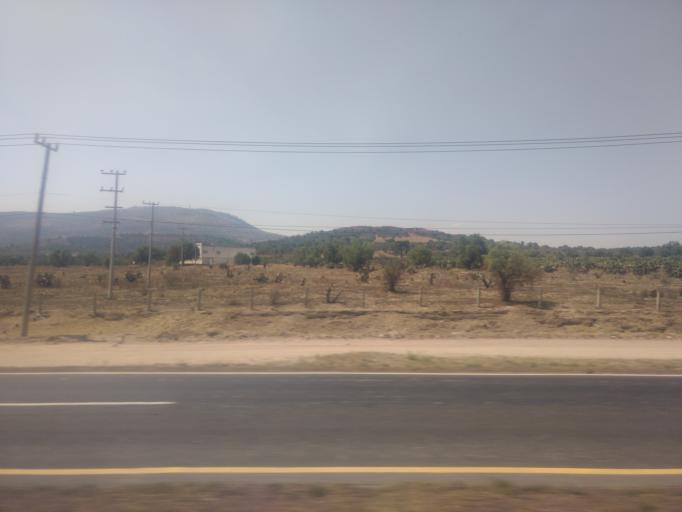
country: MX
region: Mexico
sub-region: Axapusco
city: Colonia los Remedios
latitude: 19.7339
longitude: -98.7739
